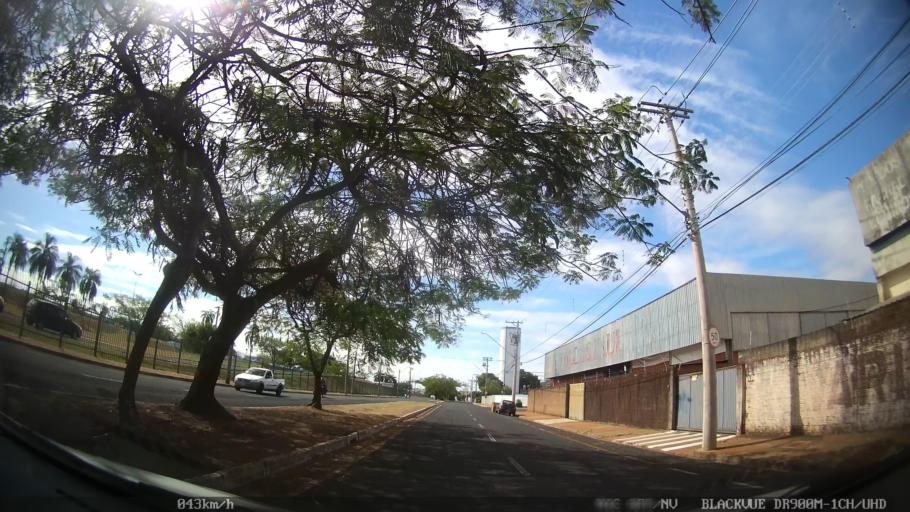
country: BR
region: Sao Paulo
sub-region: Sao Jose Do Rio Preto
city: Sao Jose do Rio Preto
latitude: -20.8348
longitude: -49.3553
